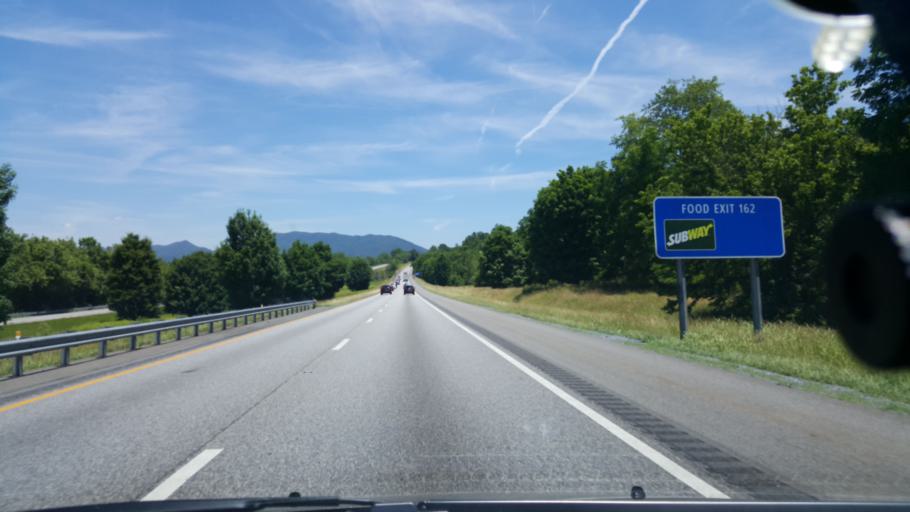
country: US
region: Virginia
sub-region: Botetourt County
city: Buchanan
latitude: 37.4871
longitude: -79.7721
